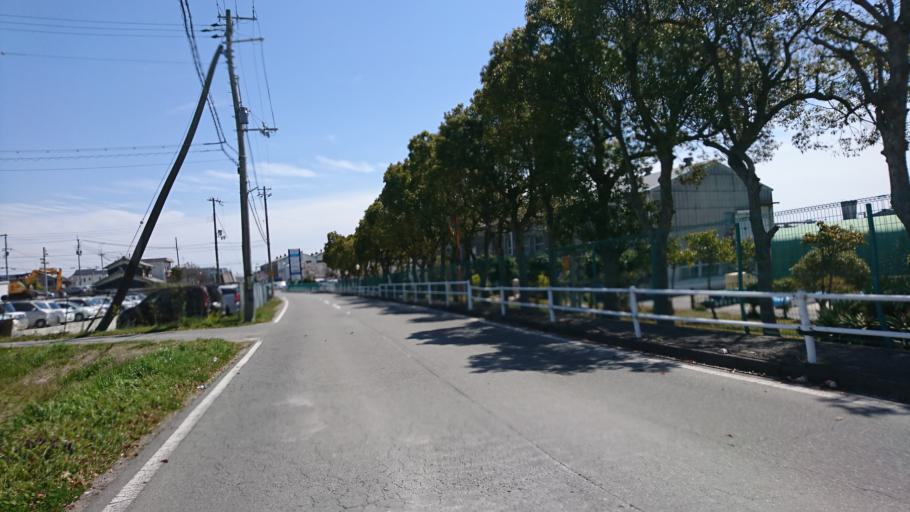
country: JP
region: Hyogo
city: Kakogawacho-honmachi
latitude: 34.7309
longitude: 134.9016
